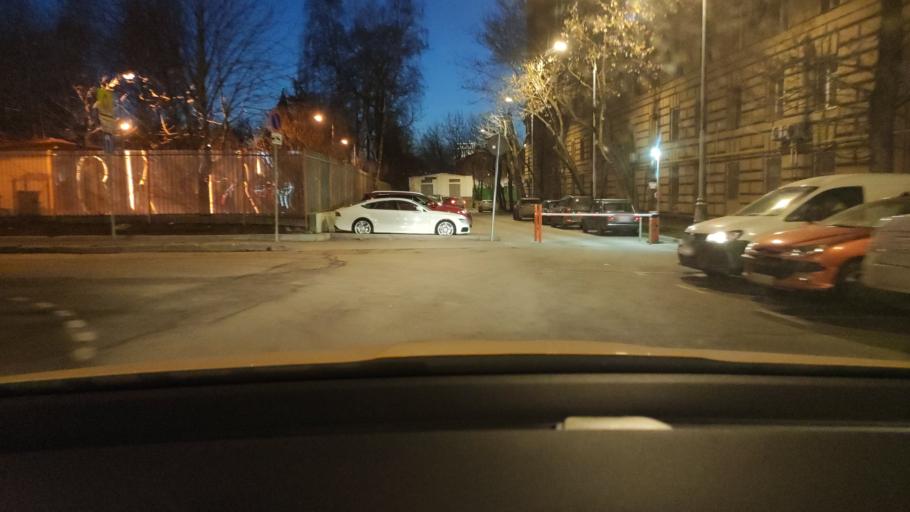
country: RU
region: Moscow
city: Taganskiy
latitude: 55.7333
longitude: 37.6577
